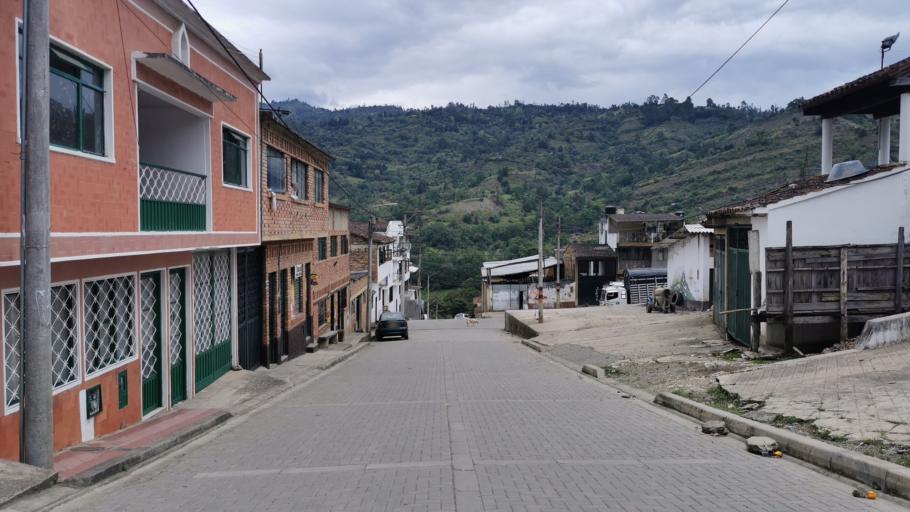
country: CO
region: Cundinamarca
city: Tenza
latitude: 5.0774
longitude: -73.4238
